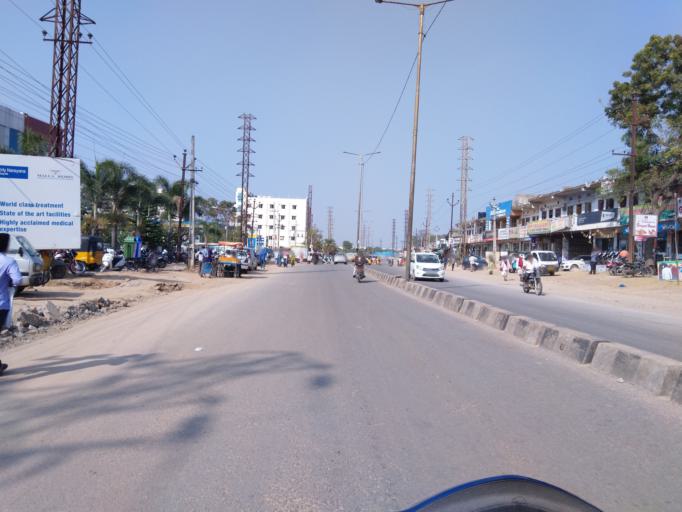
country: IN
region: Telangana
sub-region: Rangareddi
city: Quthbullapur
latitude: 17.5434
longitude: 78.4338
